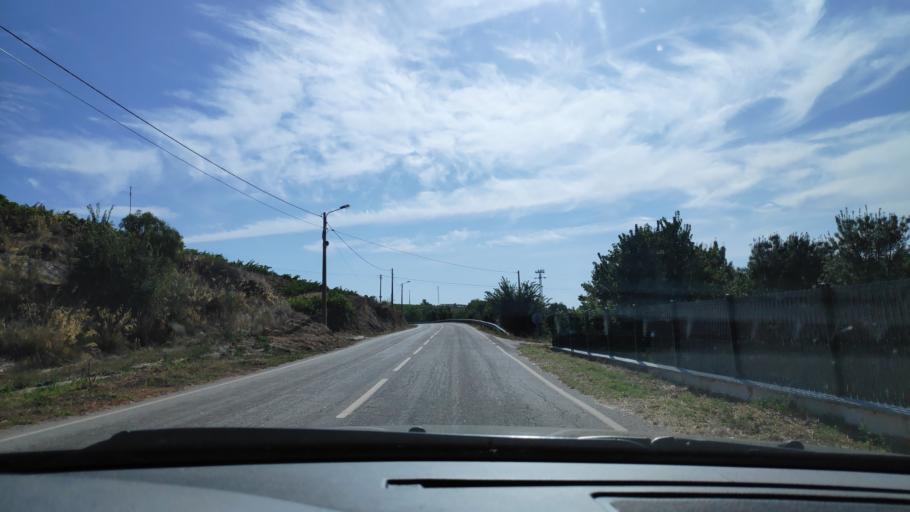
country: PT
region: Braganca
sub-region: Miranda do Douro
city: Miranda do Douro
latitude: 41.4735
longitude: -6.3445
